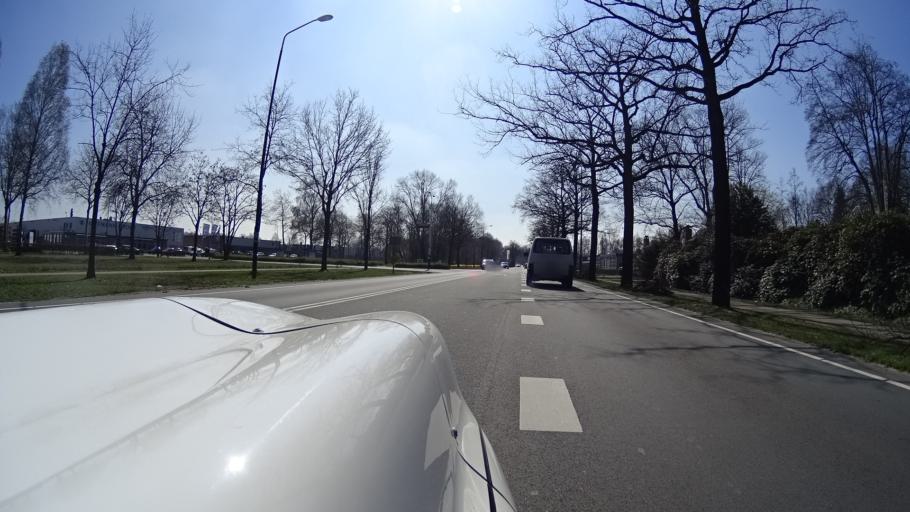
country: NL
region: North Brabant
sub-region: Gemeente Laarbeek
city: Aarle-Rixtel
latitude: 51.5230
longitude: 5.6407
